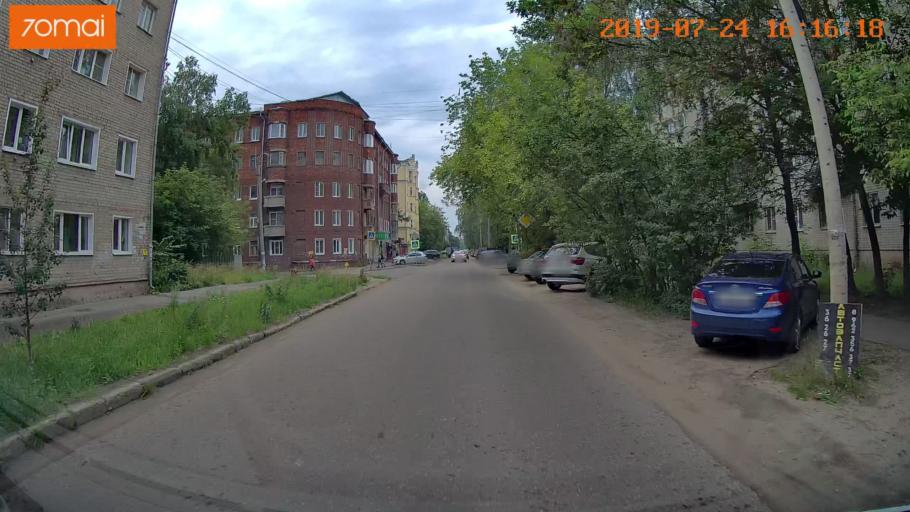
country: RU
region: Ivanovo
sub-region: Gorod Ivanovo
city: Ivanovo
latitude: 57.0062
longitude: 40.9775
